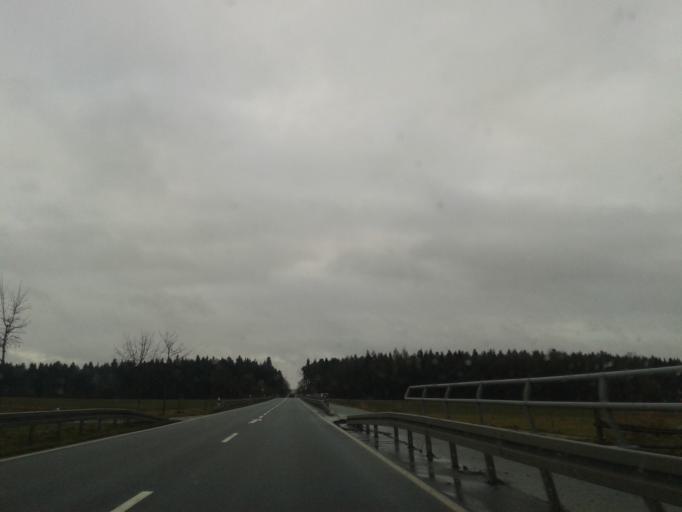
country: DE
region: Saxony
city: Durrhennersdorf
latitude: 51.0221
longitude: 14.6244
